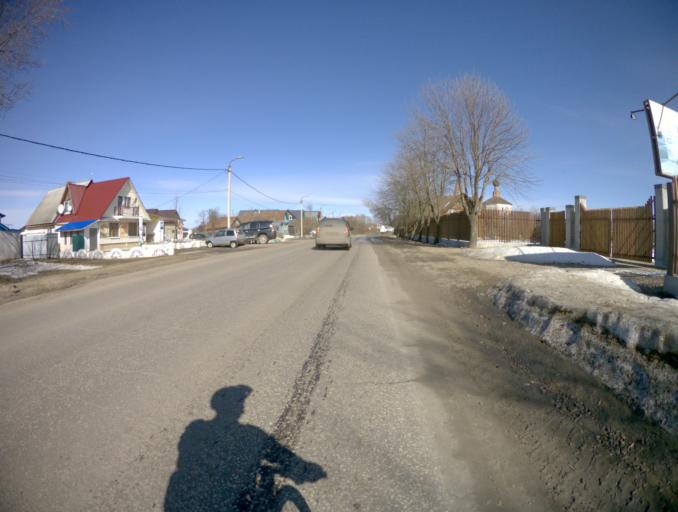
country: RU
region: Vladimir
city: Suzdal'
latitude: 56.4334
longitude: 40.4258
